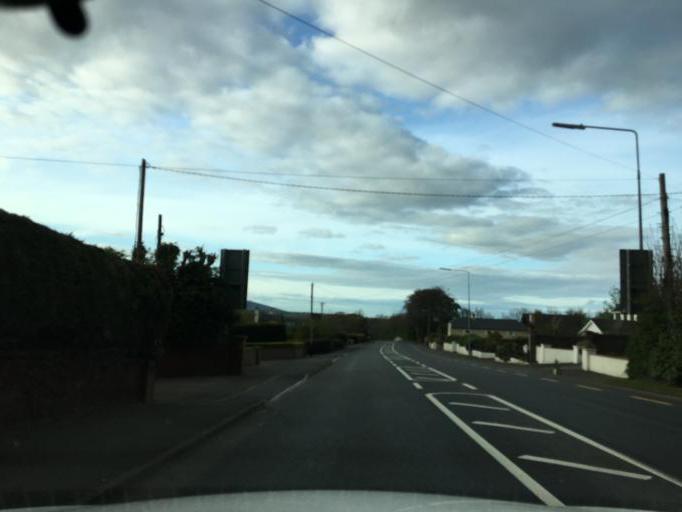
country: IE
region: Leinster
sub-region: Loch Garman
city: New Ross
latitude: 52.4095
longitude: -6.9348
